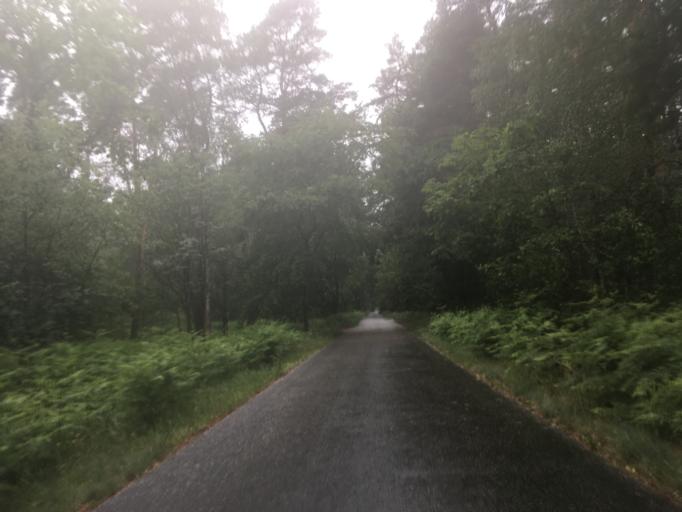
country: DE
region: Brandenburg
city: Liebenwalde
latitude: 52.8500
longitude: 13.4514
